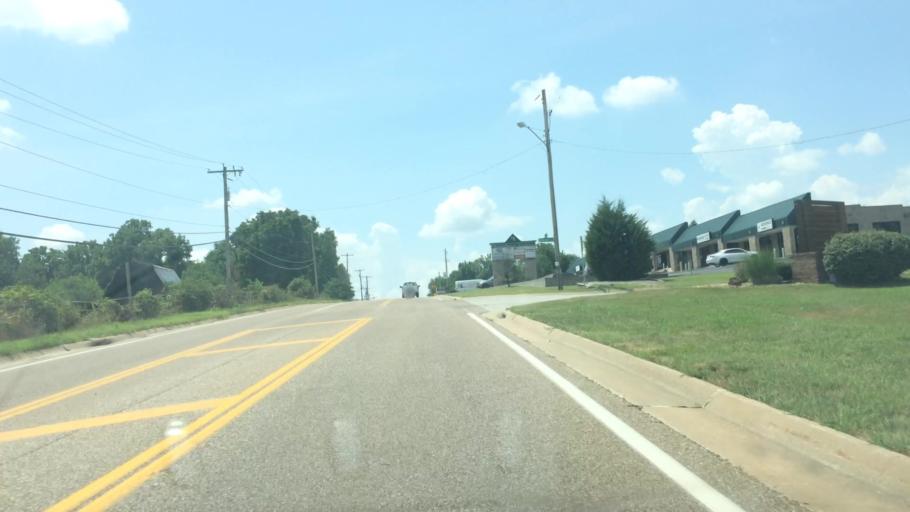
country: US
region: Missouri
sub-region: Greene County
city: Springfield
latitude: 37.2665
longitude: -93.2647
